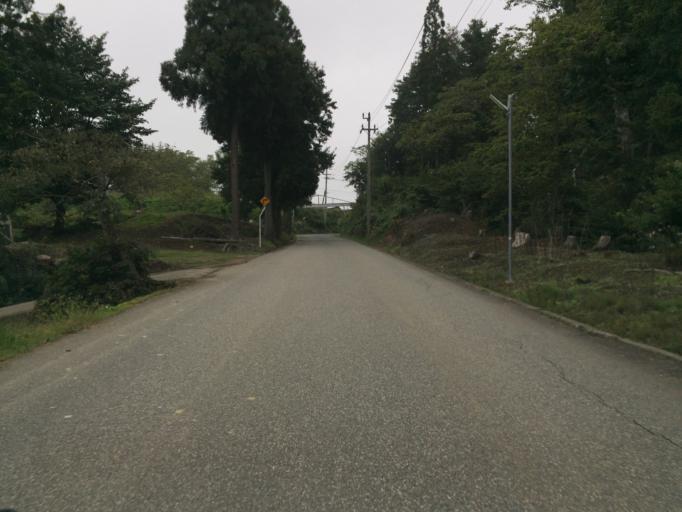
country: JP
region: Fukushima
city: Inawashiro
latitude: 37.5189
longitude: 139.9705
